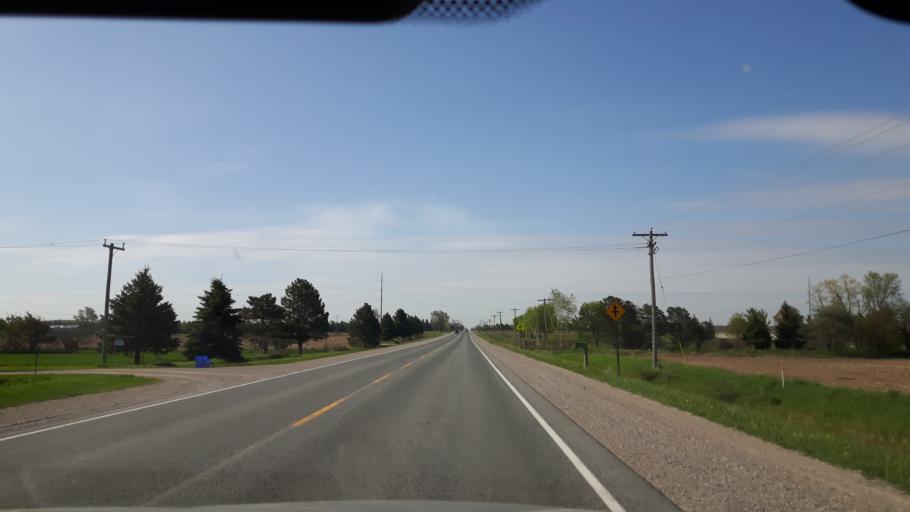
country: CA
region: Ontario
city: Bluewater
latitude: 43.5105
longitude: -81.5142
